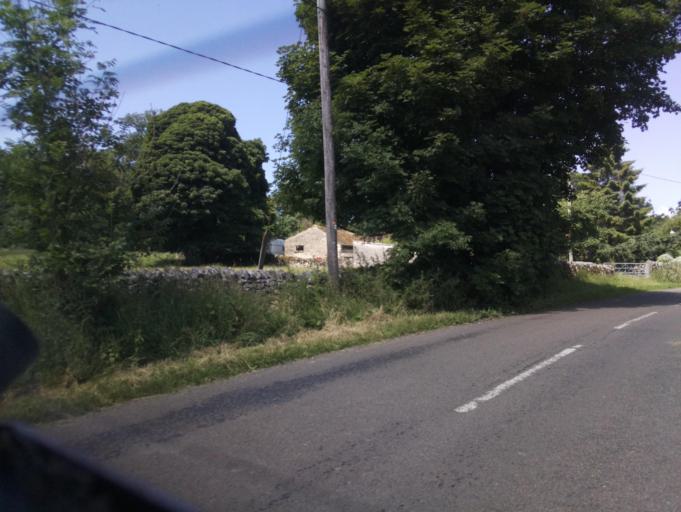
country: GB
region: England
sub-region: Derbyshire
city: Tideswell
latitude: 53.2643
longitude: -1.8171
